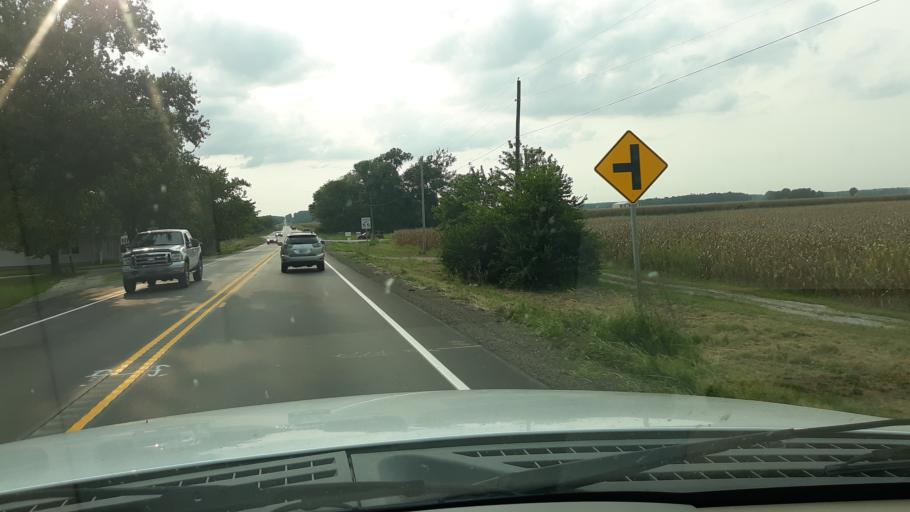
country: US
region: Indiana
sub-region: Gibson County
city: Princeton
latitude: 38.3556
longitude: -87.6233
